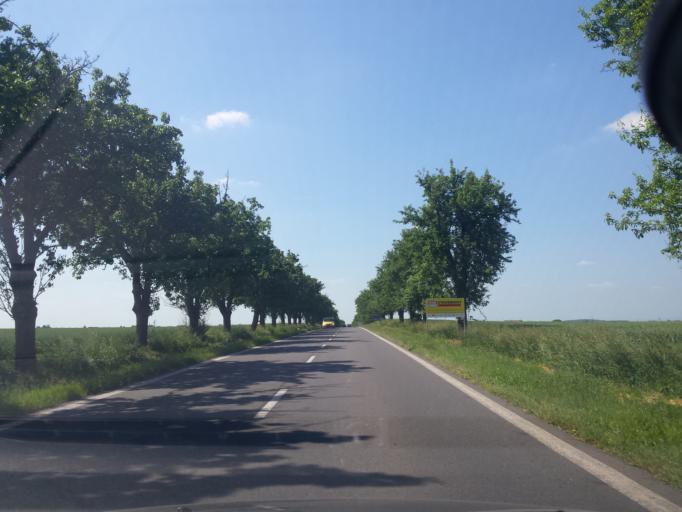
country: CZ
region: Central Bohemia
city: Horomerice
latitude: 50.1256
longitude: 14.3487
